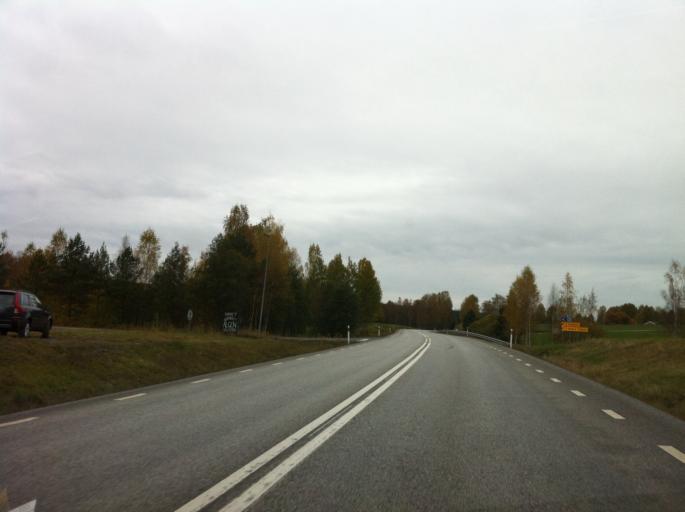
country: SE
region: OErebro
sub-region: Ljusnarsbergs Kommun
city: Kopparberg
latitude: 59.8384
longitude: 15.0927
